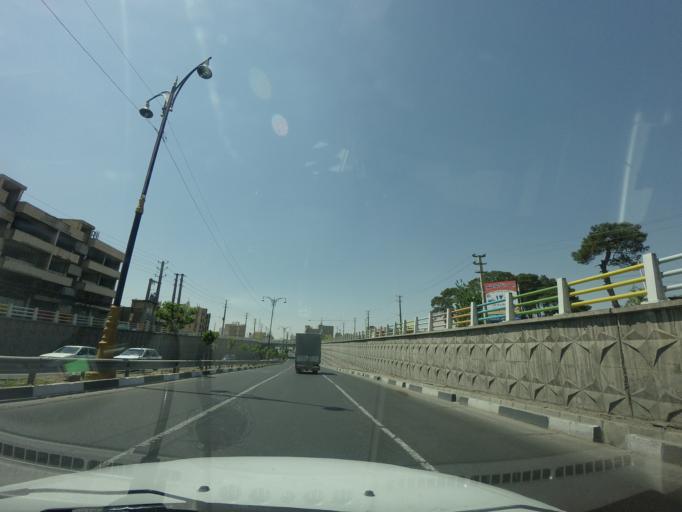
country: IR
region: Tehran
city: Eslamshahr
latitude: 35.5553
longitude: 51.2374
